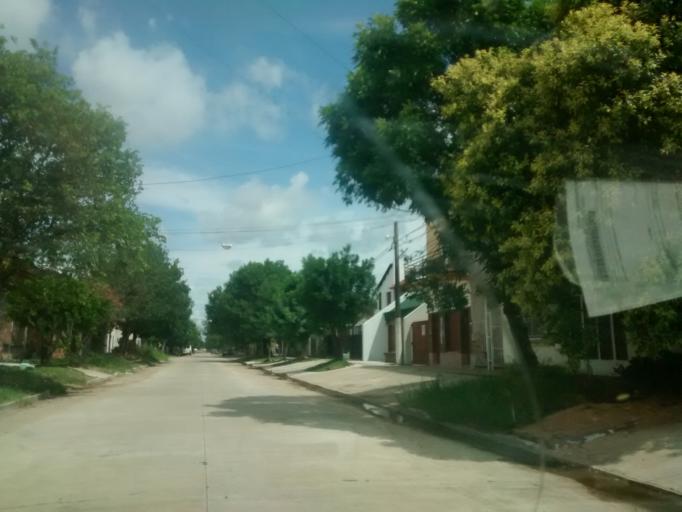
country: AR
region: Chaco
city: Resistencia
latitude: -27.4493
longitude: -58.9991
